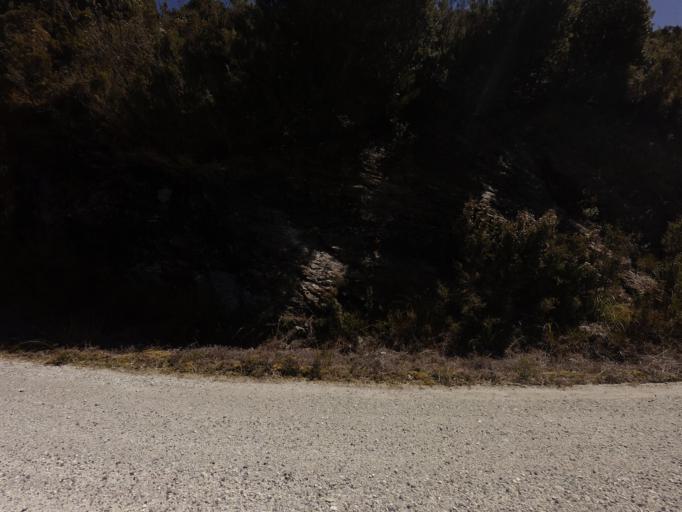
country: AU
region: Tasmania
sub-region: West Coast
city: Queenstown
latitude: -42.7744
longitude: 145.9851
